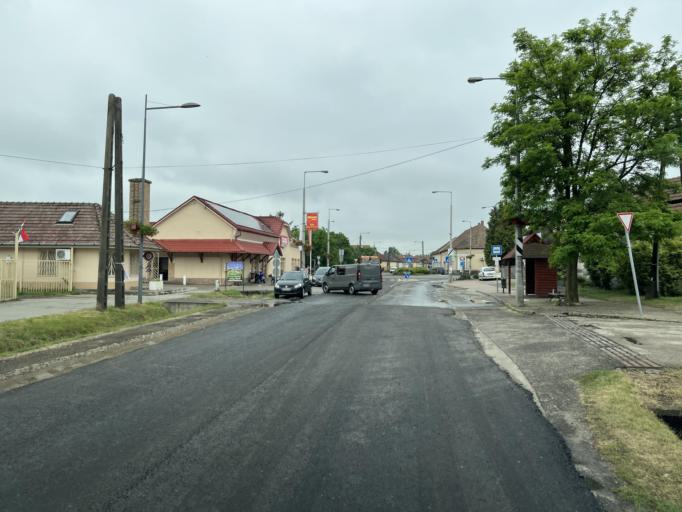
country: HU
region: Pest
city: Tura
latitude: 47.6106
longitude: 19.6012
